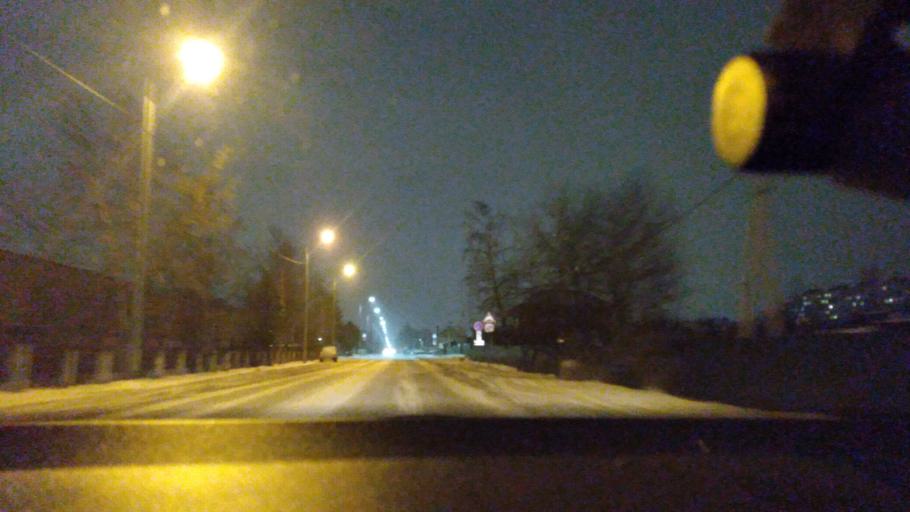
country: RU
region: Moskovskaya
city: Elektrostal'
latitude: 55.8101
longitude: 38.4411
